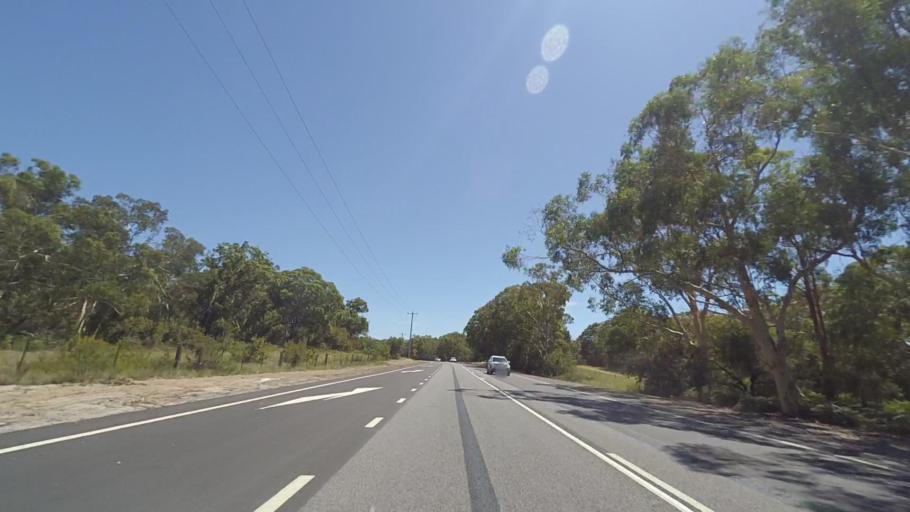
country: AU
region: New South Wales
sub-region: Port Stephens Shire
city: Medowie
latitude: -32.7818
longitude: 151.8585
